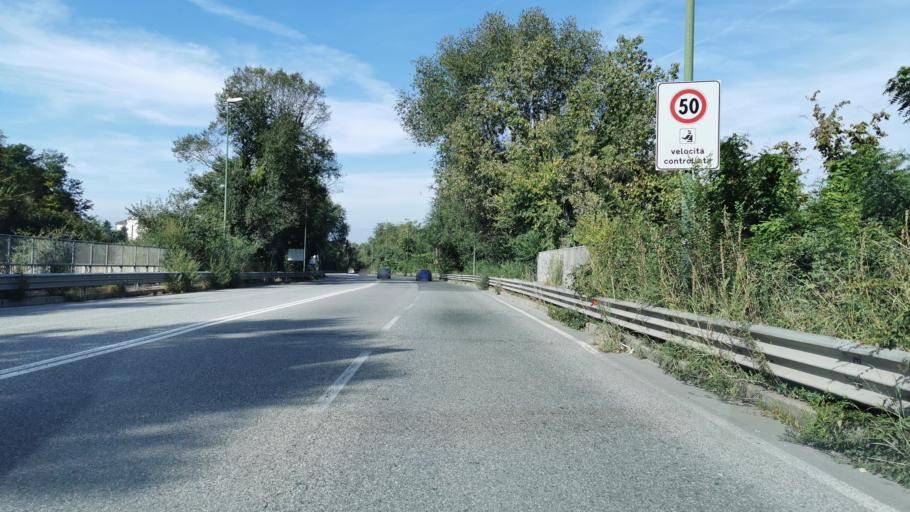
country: IT
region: Piedmont
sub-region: Provincia di Torino
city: Venaria Reale
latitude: 45.1155
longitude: 7.6622
